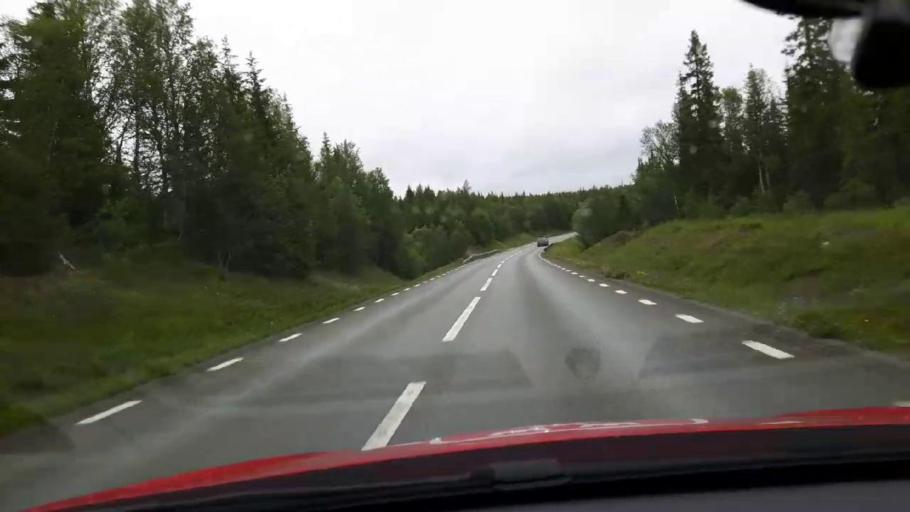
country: SE
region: Jaemtland
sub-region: Are Kommun
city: Are
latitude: 63.2970
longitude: 12.4106
